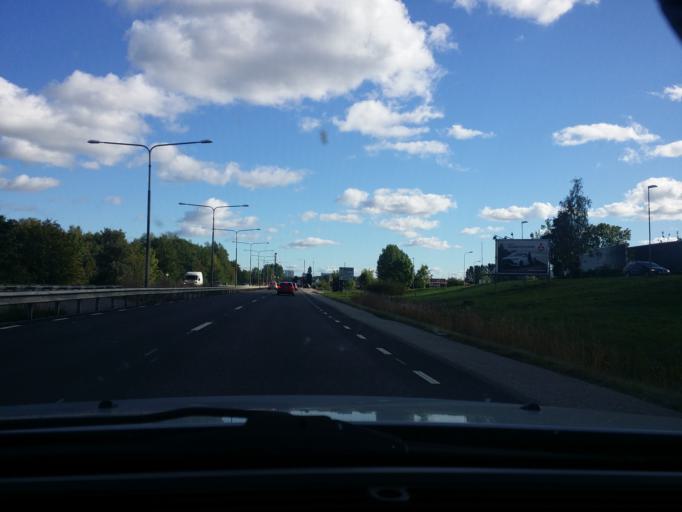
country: SE
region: Vaestmanland
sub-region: Vasteras
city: Vasteras
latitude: 59.6094
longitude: 16.4789
